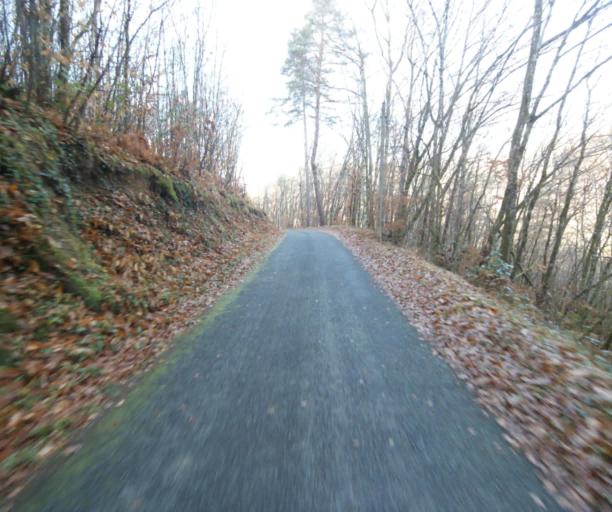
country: FR
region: Limousin
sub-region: Departement de la Correze
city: Laguenne
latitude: 45.2453
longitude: 1.7831
